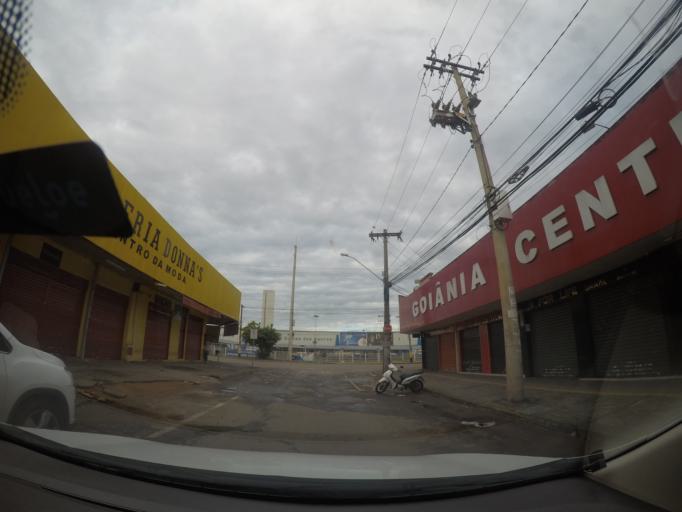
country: BR
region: Goias
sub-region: Goiania
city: Goiania
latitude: -16.6585
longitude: -49.2577
